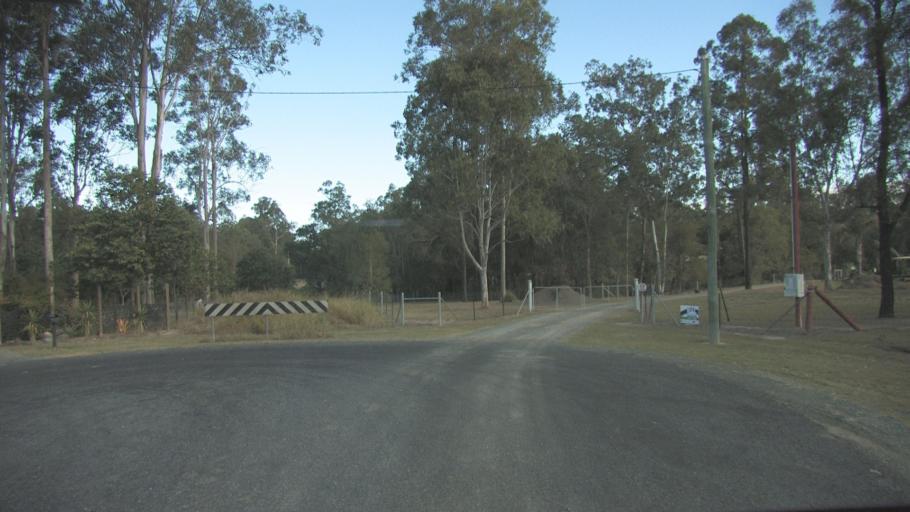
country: AU
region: Queensland
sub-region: Logan
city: North Maclean
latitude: -27.8230
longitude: 153.0487
